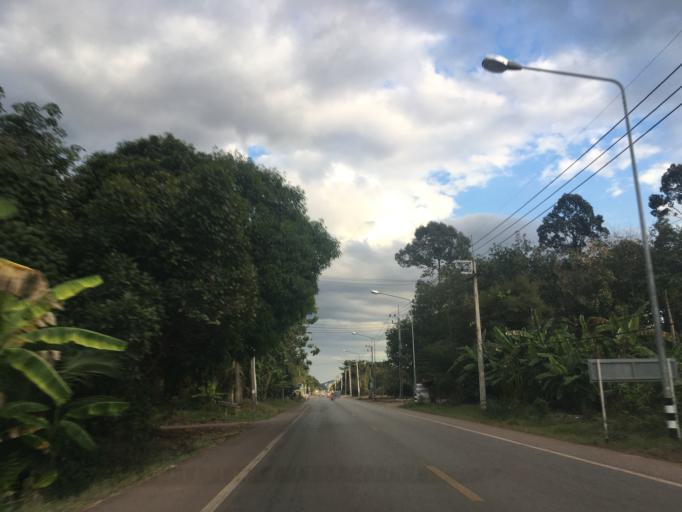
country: TH
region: Chanthaburi
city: Na Yai Am
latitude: 12.6912
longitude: 101.8112
